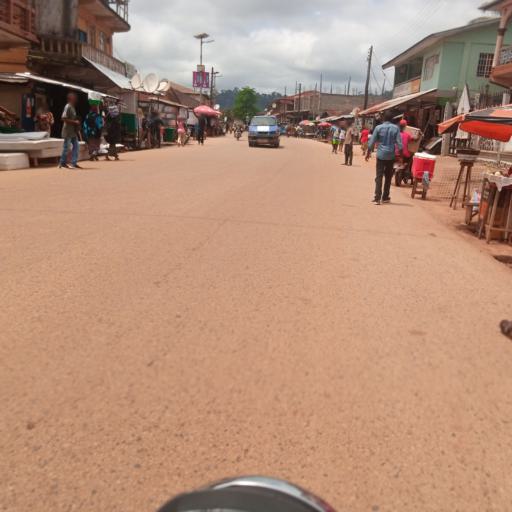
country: SL
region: Eastern Province
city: Kenema
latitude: 7.8770
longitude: -11.1886
